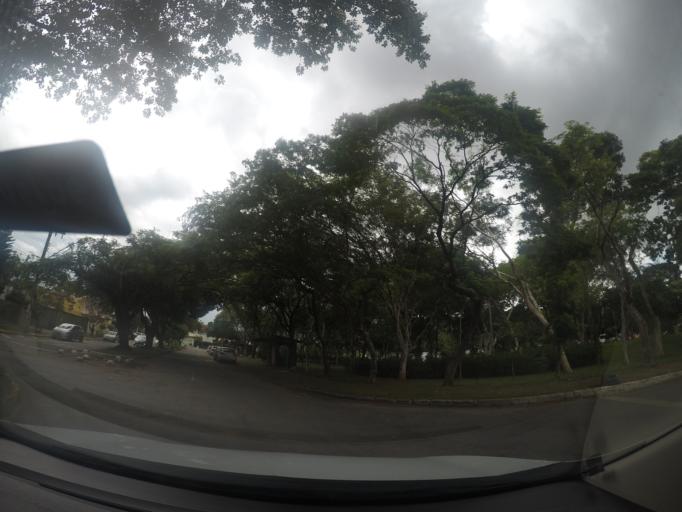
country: BR
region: Goias
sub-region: Goiania
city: Goiania
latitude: -16.6503
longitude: -49.2278
